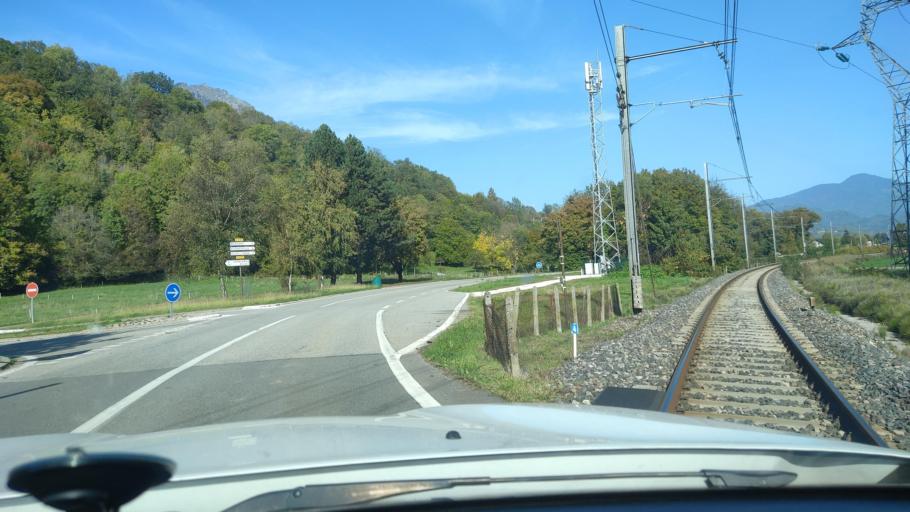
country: FR
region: Rhone-Alpes
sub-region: Departement de la Savoie
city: Frontenex
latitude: 45.6478
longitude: 6.3305
